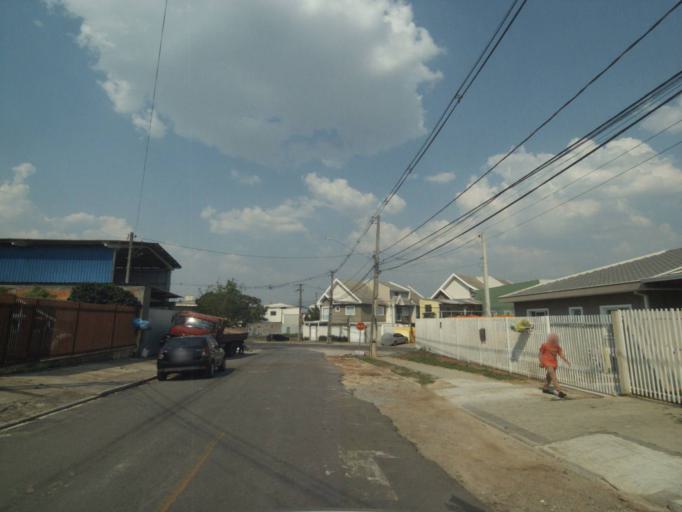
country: BR
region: Parana
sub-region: Sao Jose Dos Pinhais
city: Sao Jose dos Pinhais
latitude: -25.5351
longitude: -49.2370
